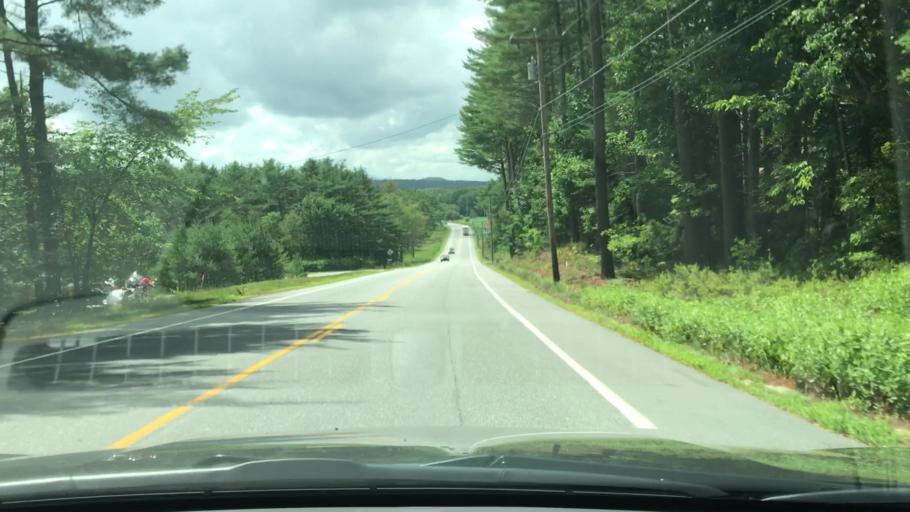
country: US
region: Maine
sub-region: Oxford County
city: Bethel
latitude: 44.4164
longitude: -70.7764
